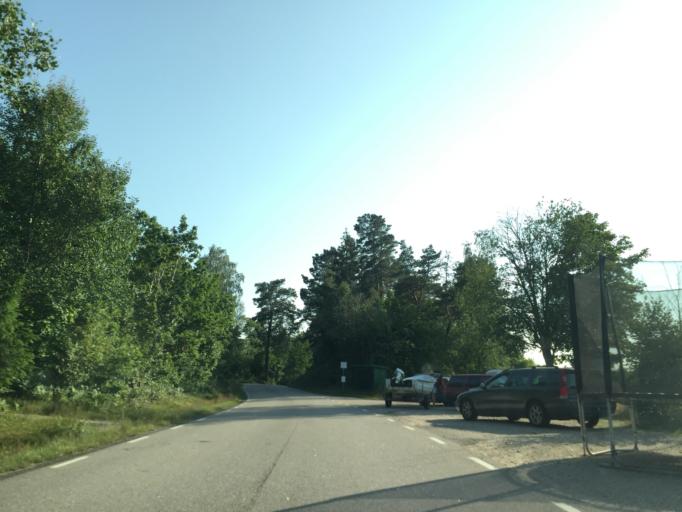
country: SE
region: Vaestra Goetaland
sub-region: Lilla Edets Kommun
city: Lilla Edet
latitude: 58.1774
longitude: 12.0947
